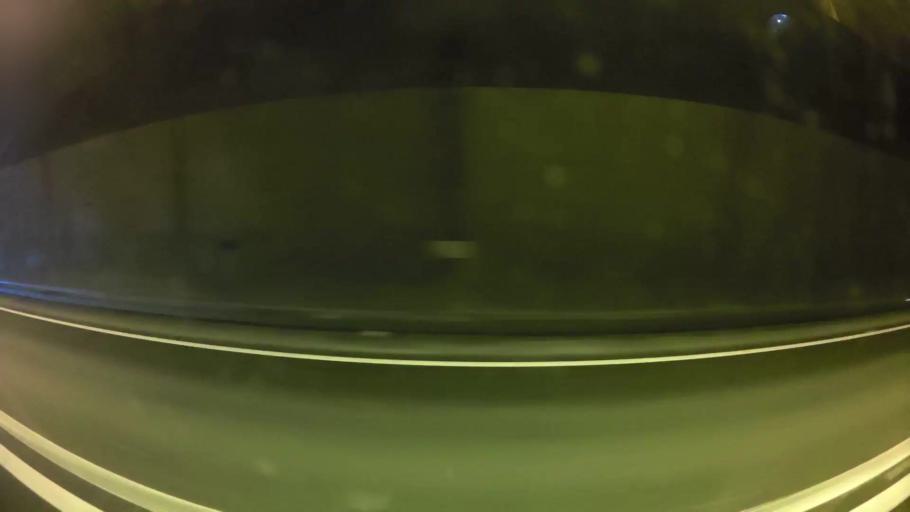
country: RS
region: Central Serbia
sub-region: Belgrade
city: Rakovica
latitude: 44.7209
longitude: 20.4557
